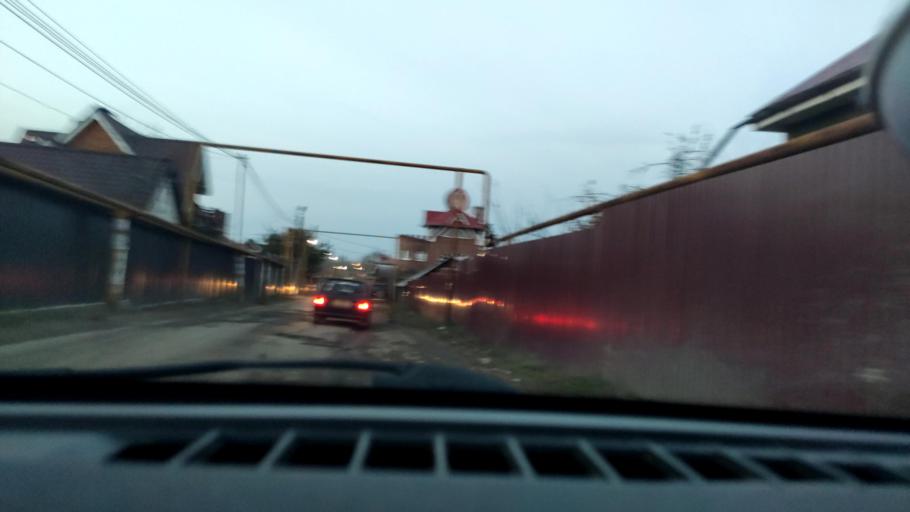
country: RU
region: Samara
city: Samara
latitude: 53.1353
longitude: 50.0952
